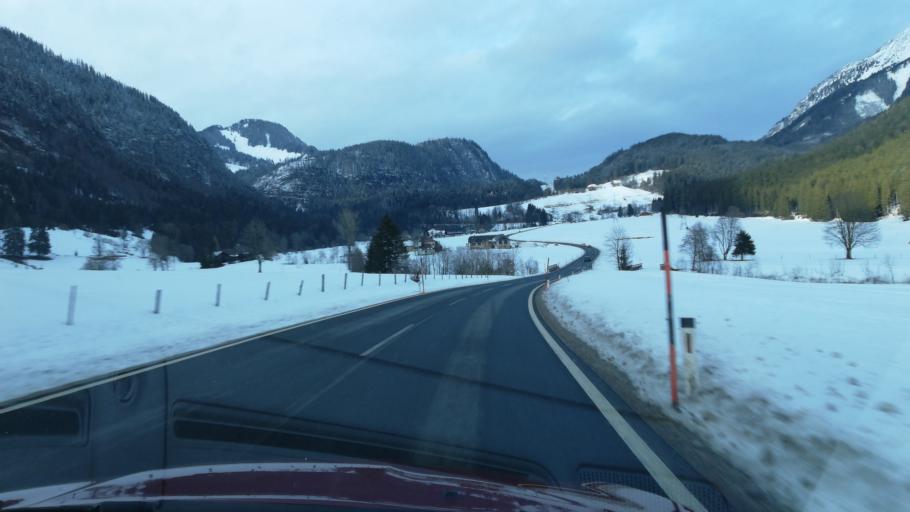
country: AT
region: Styria
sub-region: Politischer Bezirk Liezen
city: Liezen
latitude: 47.5972
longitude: 14.2812
